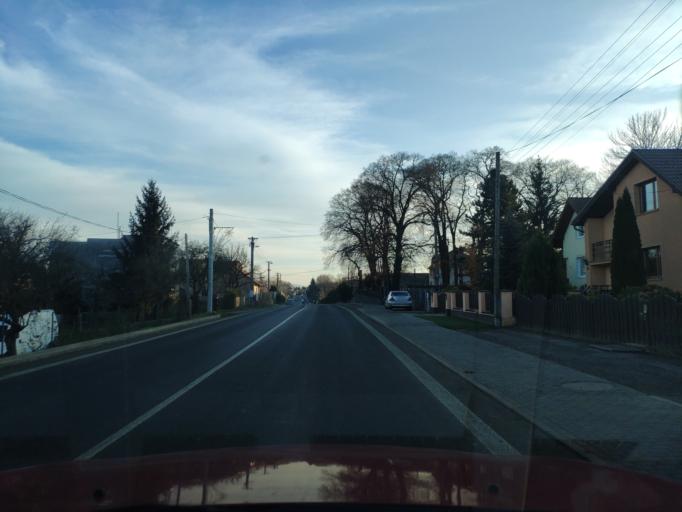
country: SK
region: Kosicky
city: Kosice
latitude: 48.8025
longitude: 21.3025
